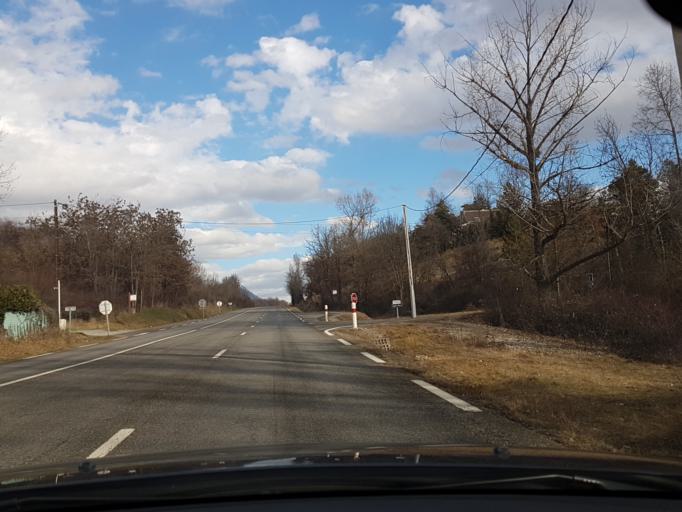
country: FR
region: Provence-Alpes-Cote d'Azur
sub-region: Departement des Hautes-Alpes
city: Tallard
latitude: 44.4763
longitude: 6.0347
